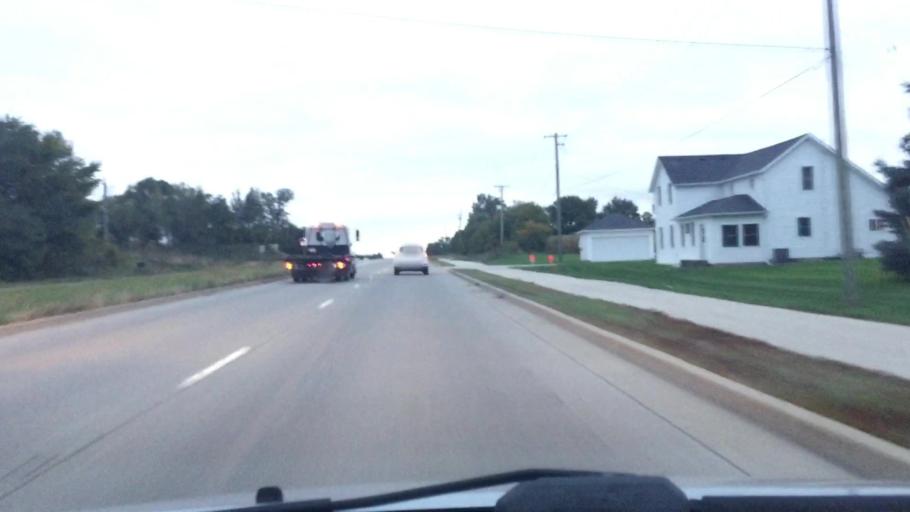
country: US
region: Illinois
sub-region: McHenry County
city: Algonquin
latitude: 42.1983
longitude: -88.2864
